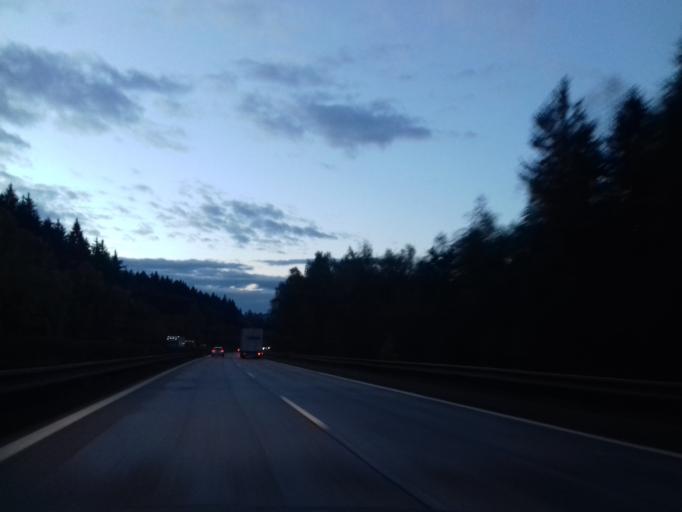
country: CZ
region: Central Bohemia
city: Divisov
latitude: 49.8106
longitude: 14.8853
